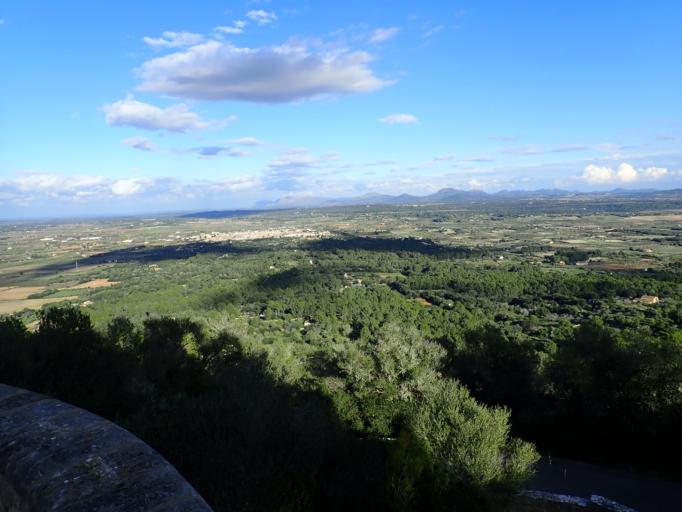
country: ES
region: Balearic Islands
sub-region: Illes Balears
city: Vilafranca de Bonany
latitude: 39.5955
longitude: 3.0893
